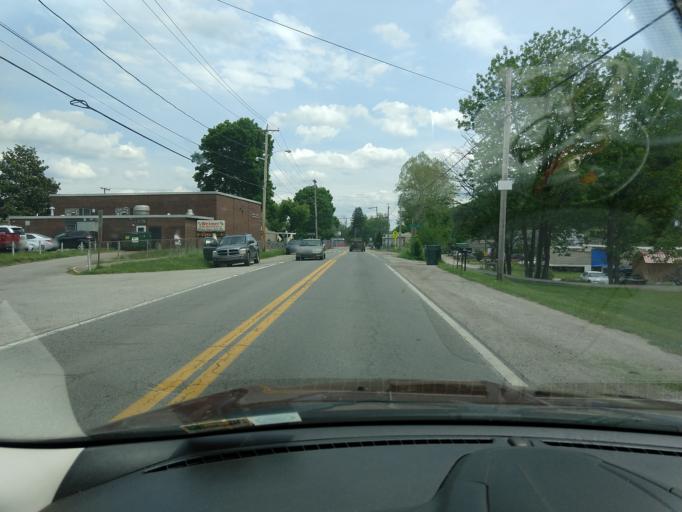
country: US
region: West Virginia
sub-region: Kanawha County
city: Cross Lanes
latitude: 38.3751
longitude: -81.7897
